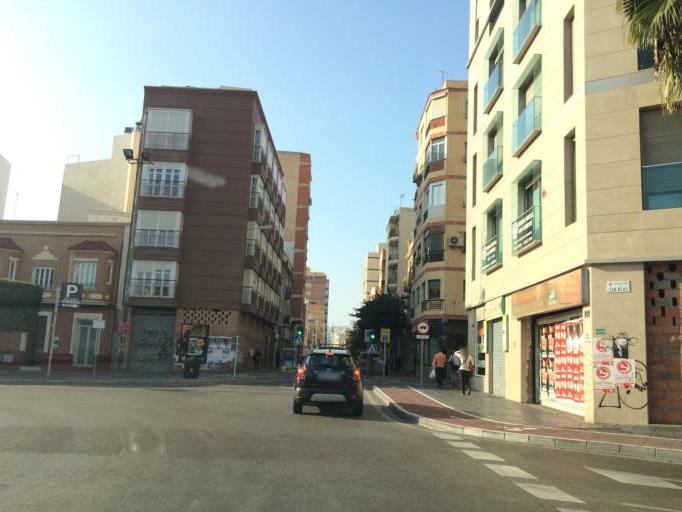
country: ES
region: Andalusia
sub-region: Provincia de Almeria
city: Almeria
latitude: 36.8461
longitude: -2.4593
